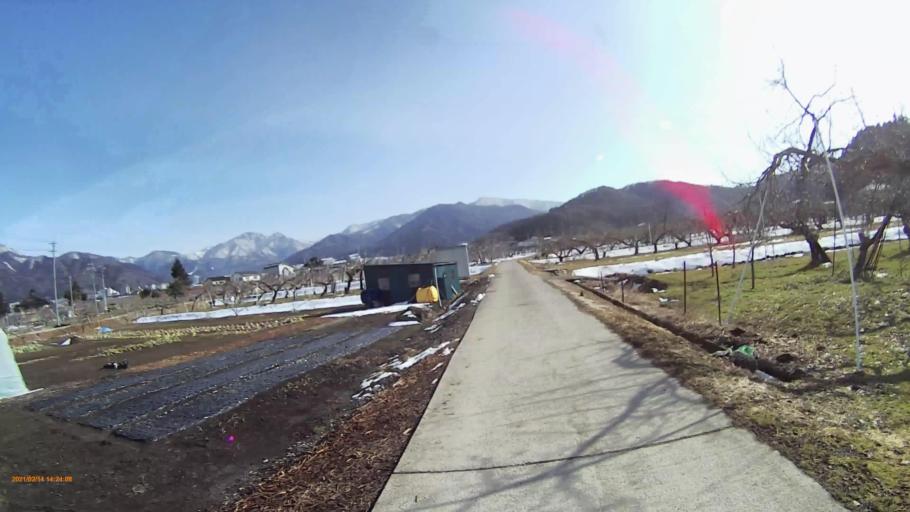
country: JP
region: Nagano
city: Nakano
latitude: 36.7457
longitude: 138.3941
